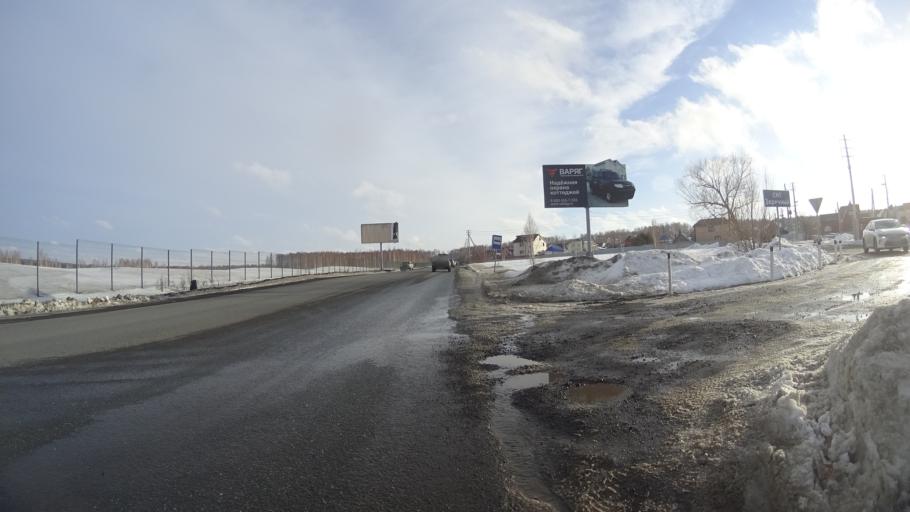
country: RU
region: Chelyabinsk
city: Sargazy
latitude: 55.1340
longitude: 61.2859
